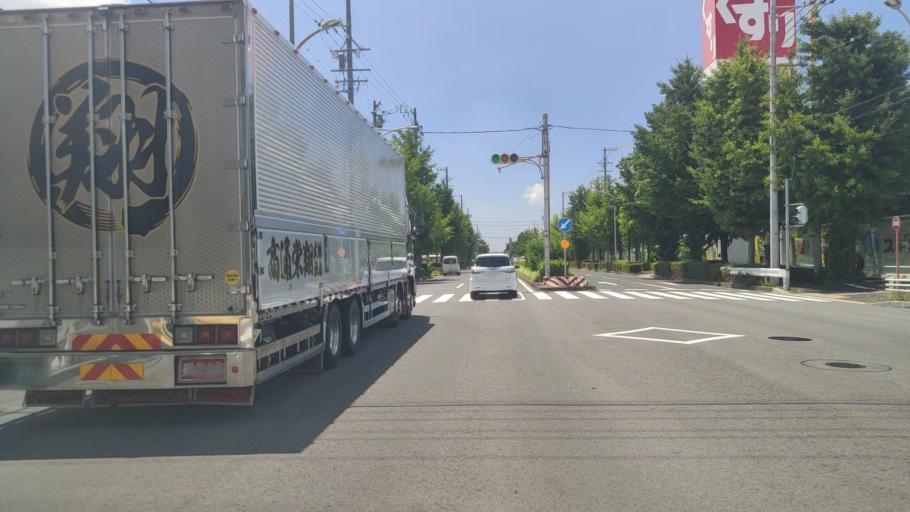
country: JP
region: Aichi
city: Kanie
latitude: 35.1341
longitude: 136.8448
